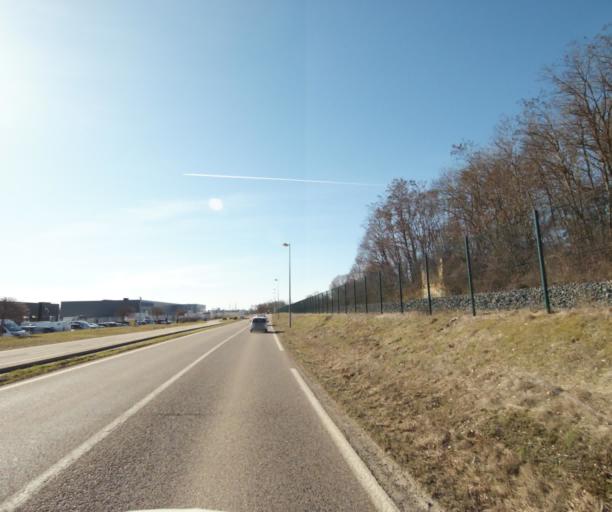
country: FR
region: Lorraine
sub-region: Departement de Meurthe-et-Moselle
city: Ludres
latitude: 48.6277
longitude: 6.1800
